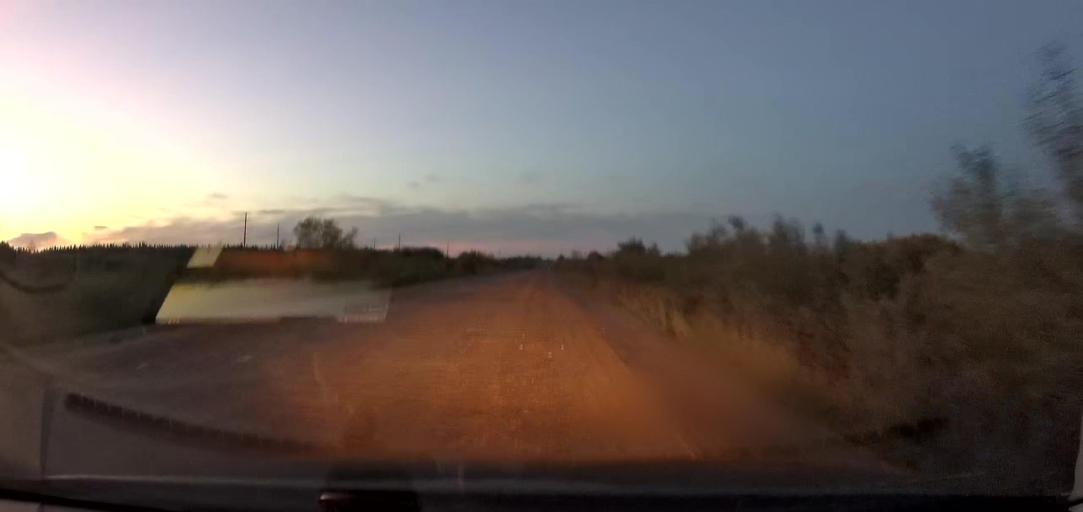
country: RU
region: Arkhangelskaya
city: Kholmogory
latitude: 64.3302
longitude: 41.4484
